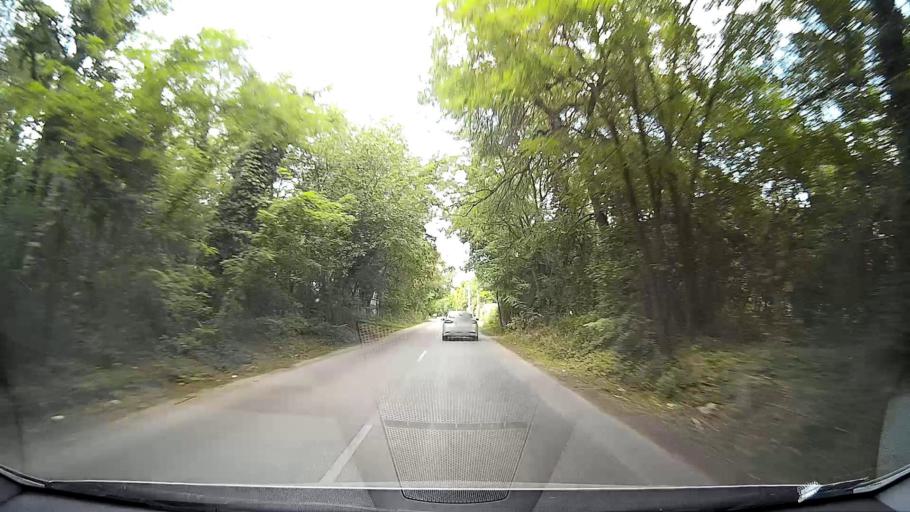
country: HU
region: Pest
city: Tahitotfalu
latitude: 47.7432
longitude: 19.0989
